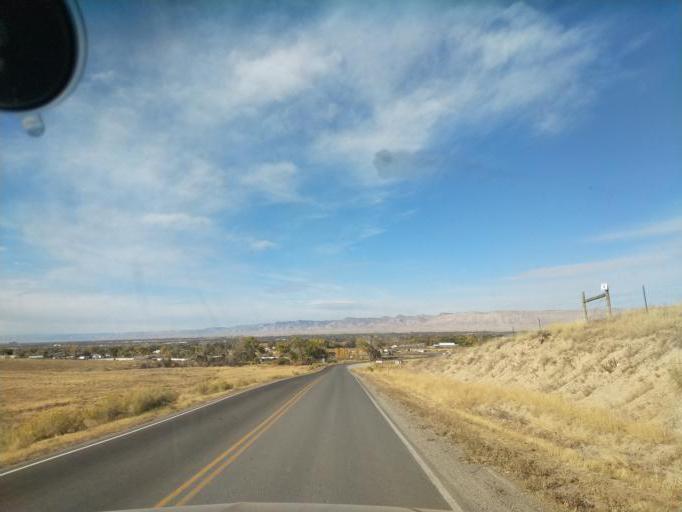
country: US
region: Colorado
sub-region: Mesa County
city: Fruitvale
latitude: 39.0161
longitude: -108.4844
